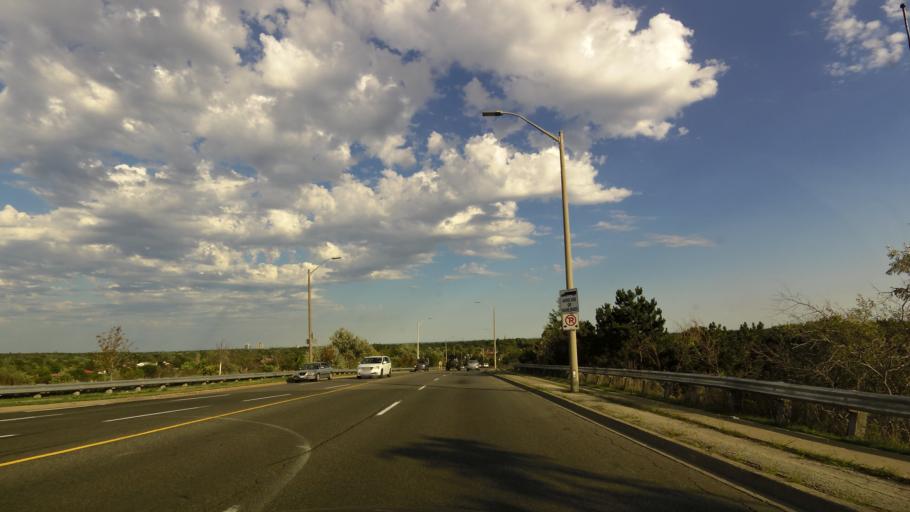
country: CA
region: Ontario
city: Mississauga
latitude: 43.5654
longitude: -79.6323
